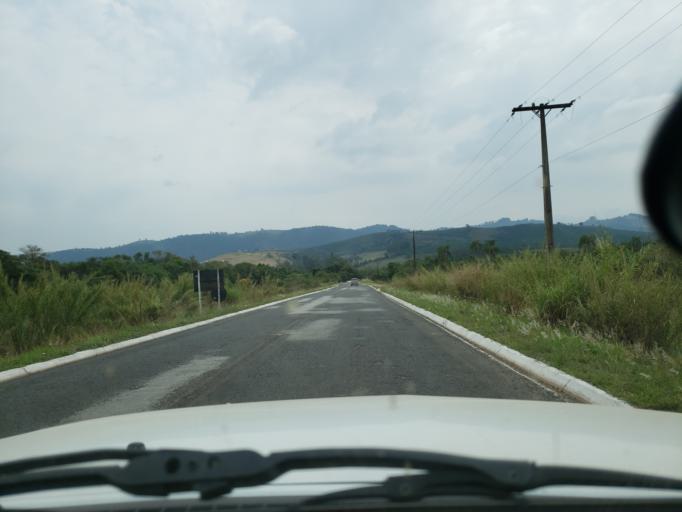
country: BR
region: Minas Gerais
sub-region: Jacutinga
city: Jacutinga
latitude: -22.2726
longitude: -46.6041
